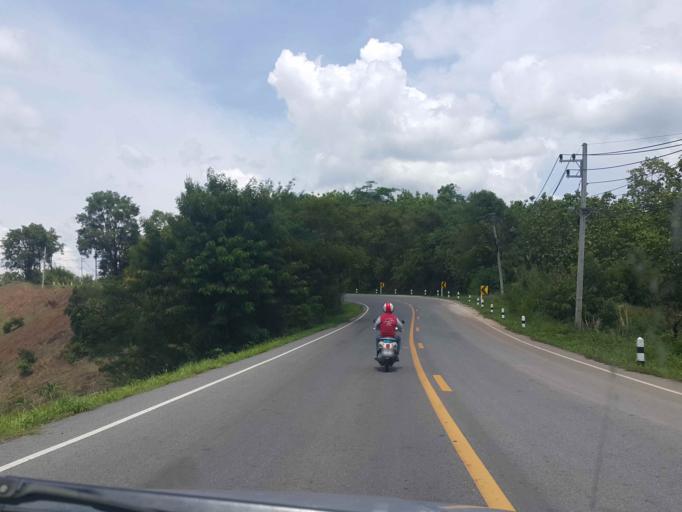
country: TH
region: Nan
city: Ban Luang
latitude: 18.8621
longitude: 100.4598
